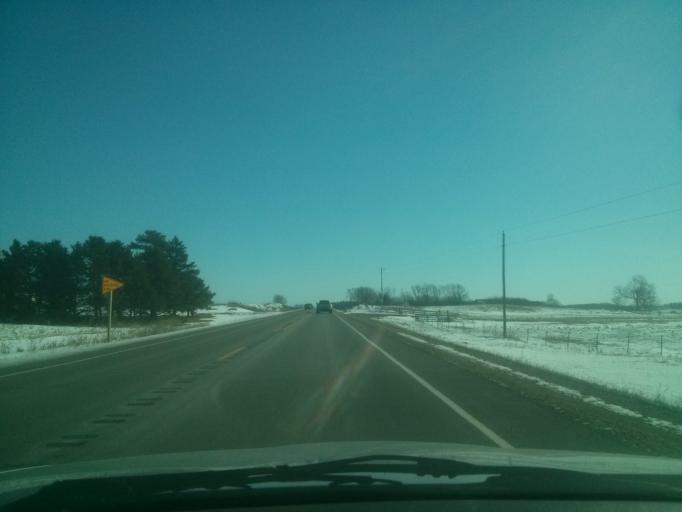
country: US
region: Wisconsin
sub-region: Polk County
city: Clear Lake
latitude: 45.1365
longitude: -92.3010
